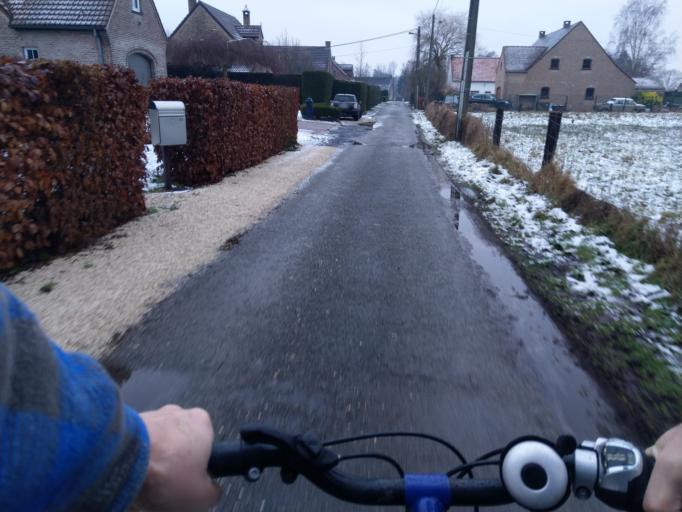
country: BE
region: Wallonia
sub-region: Province du Hainaut
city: Jurbise
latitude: 50.5119
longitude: 3.9467
